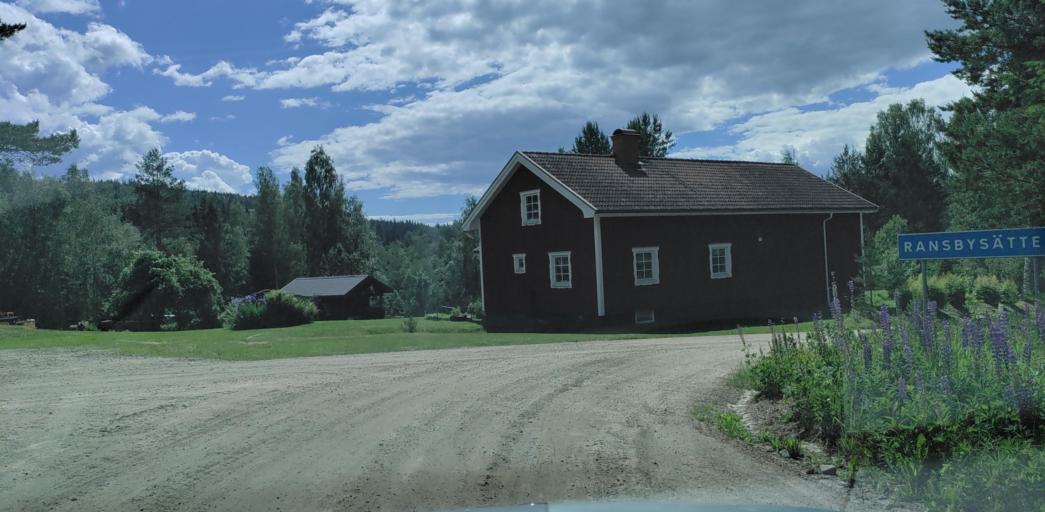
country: SE
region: Vaermland
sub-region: Sunne Kommun
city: Sunne
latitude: 60.0363
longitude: 13.2434
